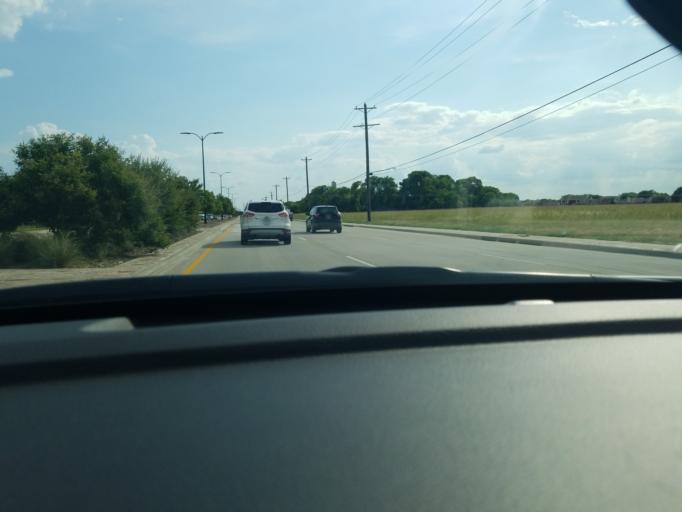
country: US
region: Texas
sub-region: Denton County
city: Little Elm
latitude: 33.1665
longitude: -96.9286
